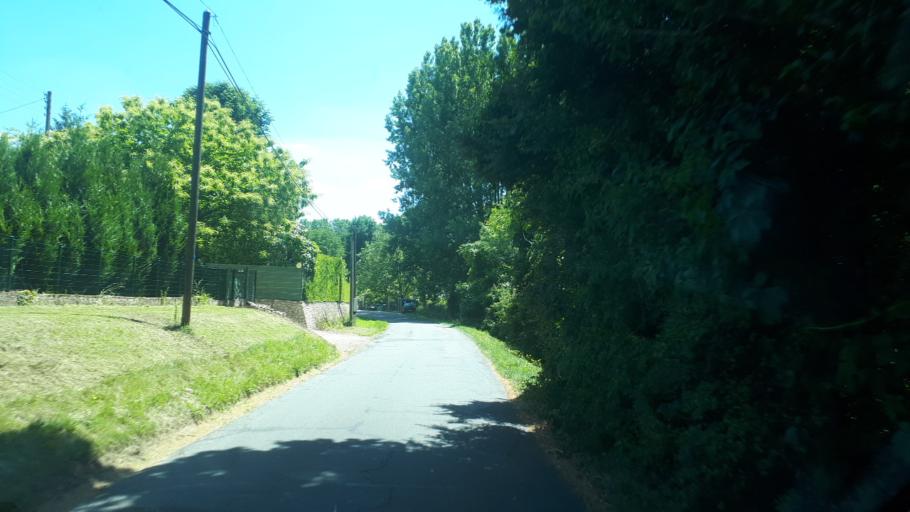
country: FR
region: Centre
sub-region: Departement du Loir-et-Cher
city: Saint-Sulpice-de-Pommeray
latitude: 47.5868
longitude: 1.2078
